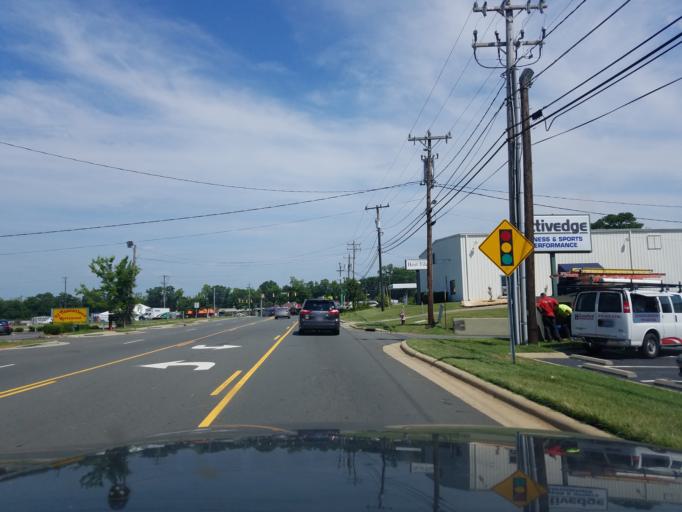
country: US
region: North Carolina
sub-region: Durham County
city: Durham
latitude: 35.9601
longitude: -78.9758
